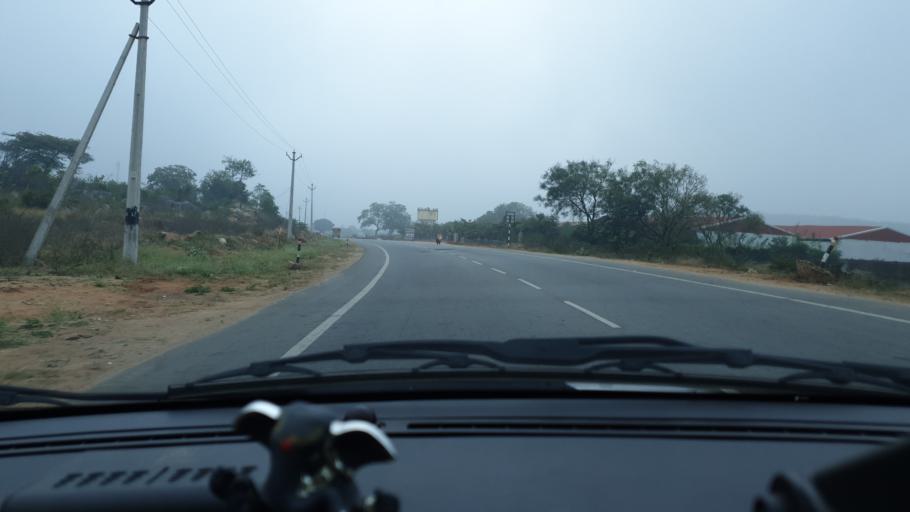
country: IN
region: Telangana
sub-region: Mahbubnagar
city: Farrukhnagar
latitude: 16.9569
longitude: 78.5140
